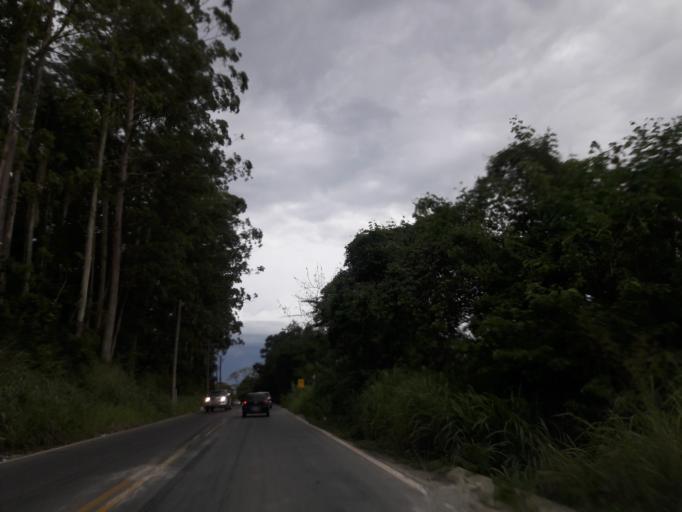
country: BR
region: Sao Paulo
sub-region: Aruja
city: Aruja
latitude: -23.3876
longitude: -46.4129
